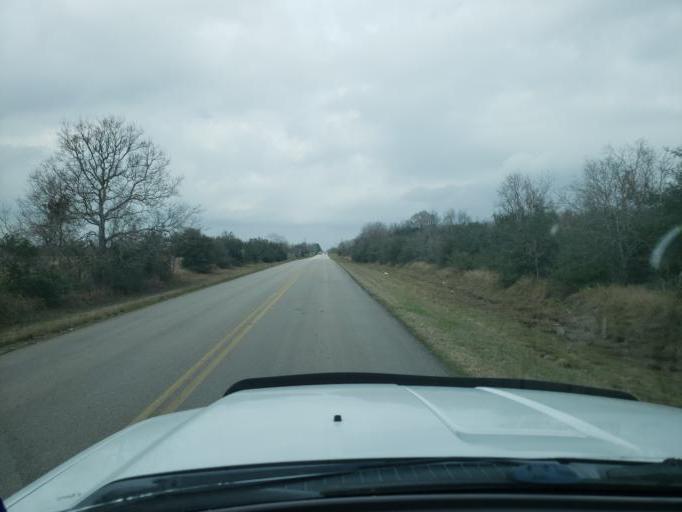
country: US
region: Texas
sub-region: Fort Bend County
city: Needville
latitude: 29.3715
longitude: -95.7320
